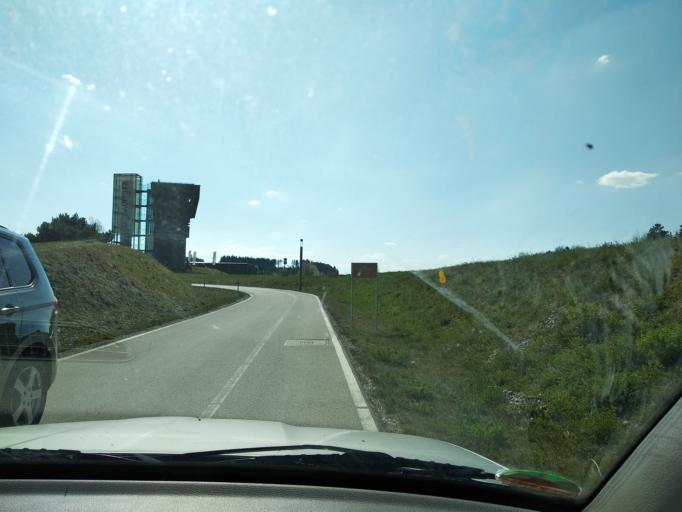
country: DE
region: Bavaria
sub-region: Swabia
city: Erkheim
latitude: 48.0290
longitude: 10.3345
